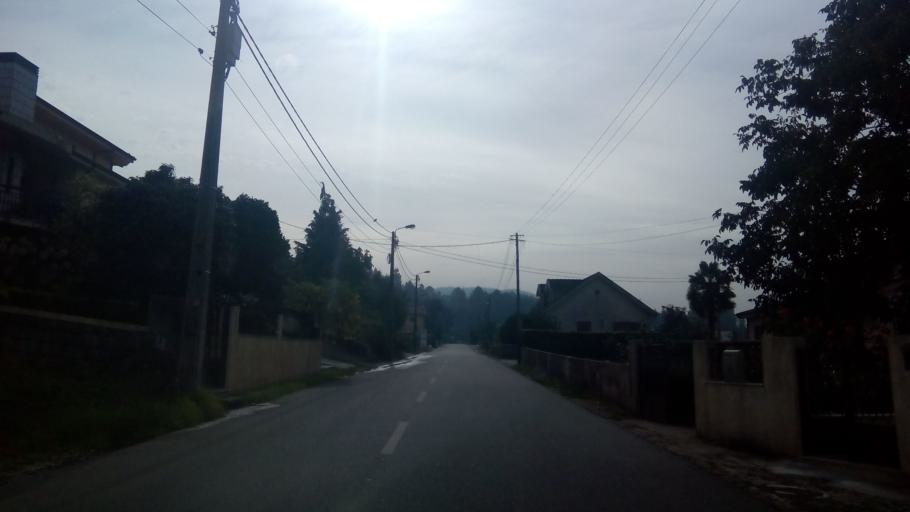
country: PT
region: Porto
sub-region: Paredes
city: Gandra
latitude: 41.1902
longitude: -8.4276
